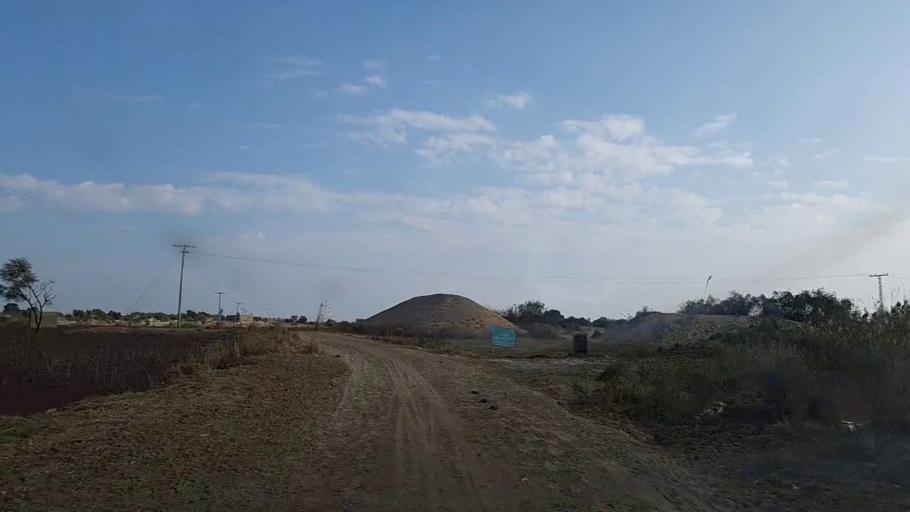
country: PK
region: Sindh
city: Sanghar
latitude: 26.2044
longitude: 69.0222
